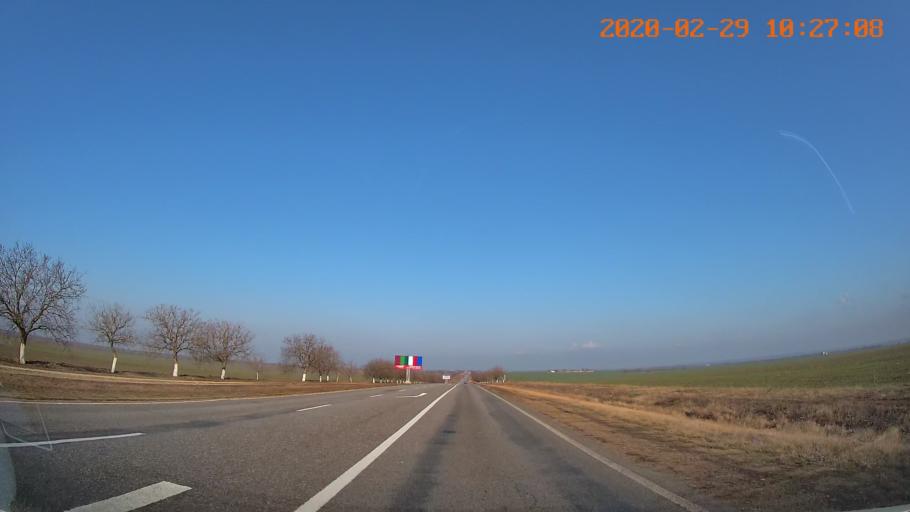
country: MD
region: Telenesti
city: Tiraspolul Nou
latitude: 46.8920
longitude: 29.5995
